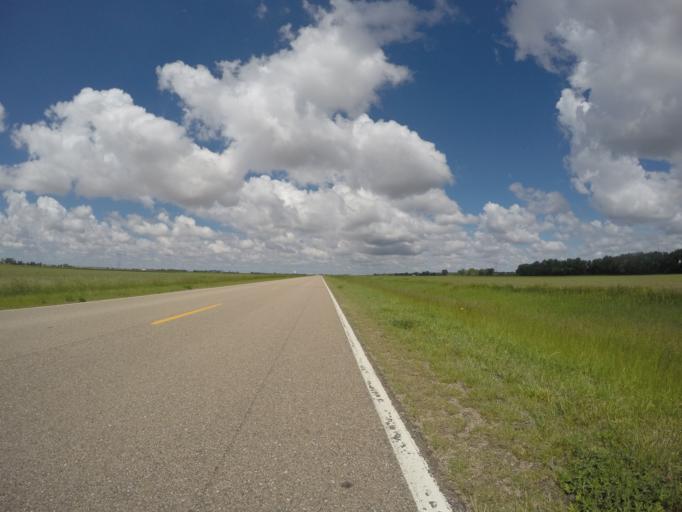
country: US
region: Nebraska
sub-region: Buffalo County
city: Kearney
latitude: 40.6569
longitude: -99.2499
